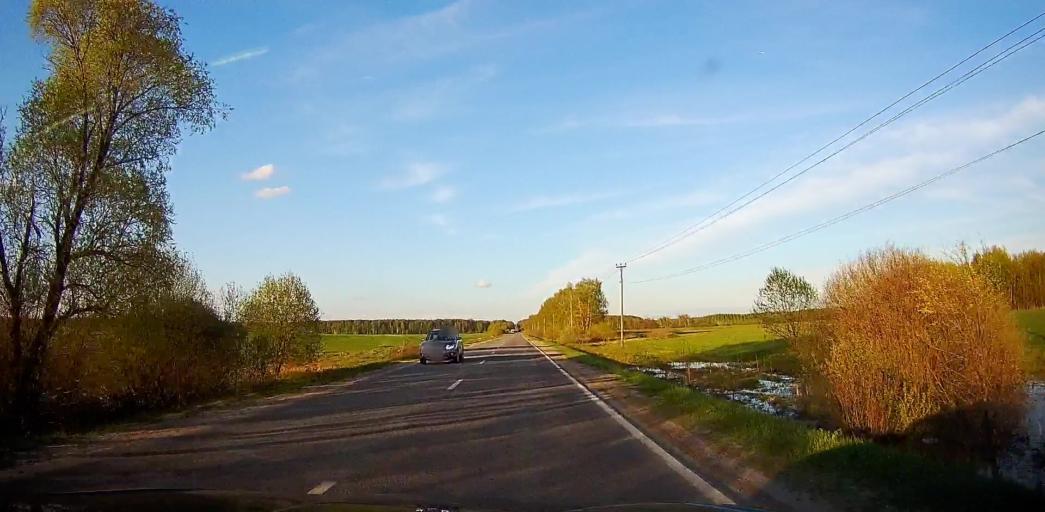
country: RU
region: Moskovskaya
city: Bronnitsy
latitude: 55.2867
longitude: 38.1860
